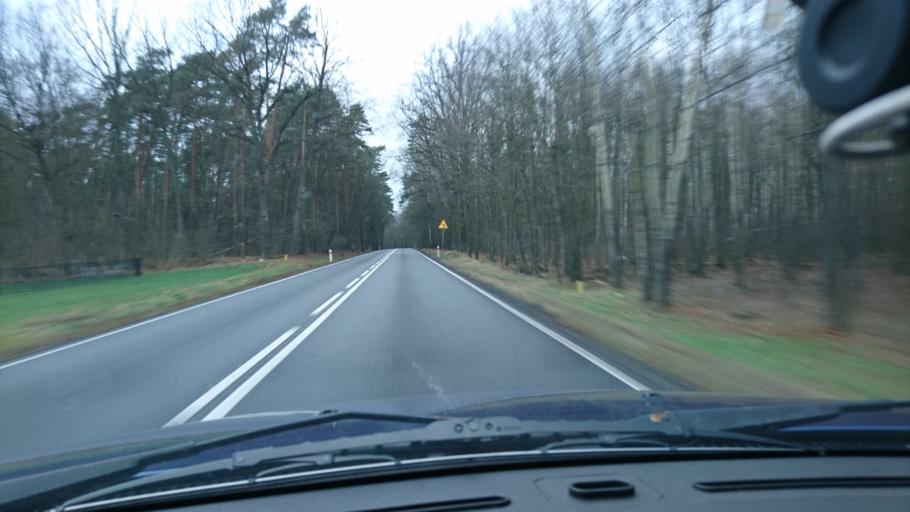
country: PL
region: Opole Voivodeship
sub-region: Powiat kluczborski
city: Kluczbork
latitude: 50.9425
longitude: 18.3238
